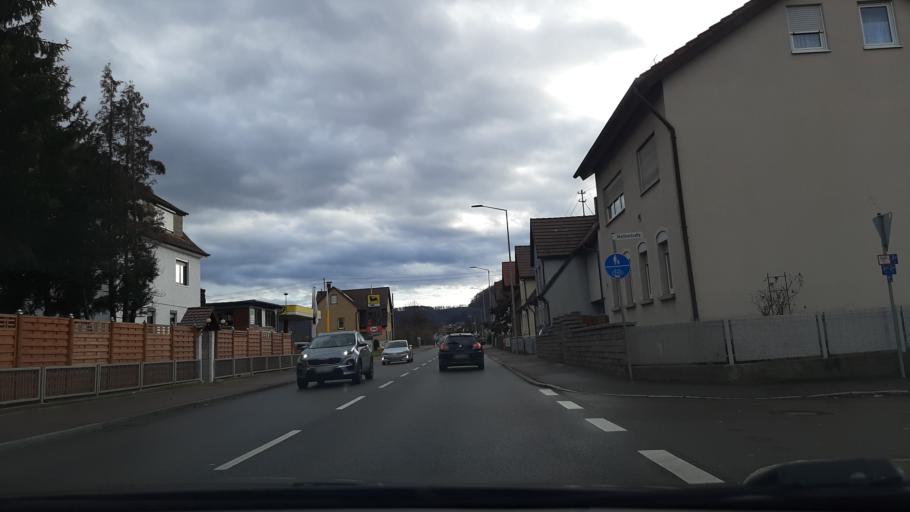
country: DE
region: Baden-Wuerttemberg
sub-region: Regierungsbezirk Stuttgart
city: Kuchen
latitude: 48.6332
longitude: 9.8038
